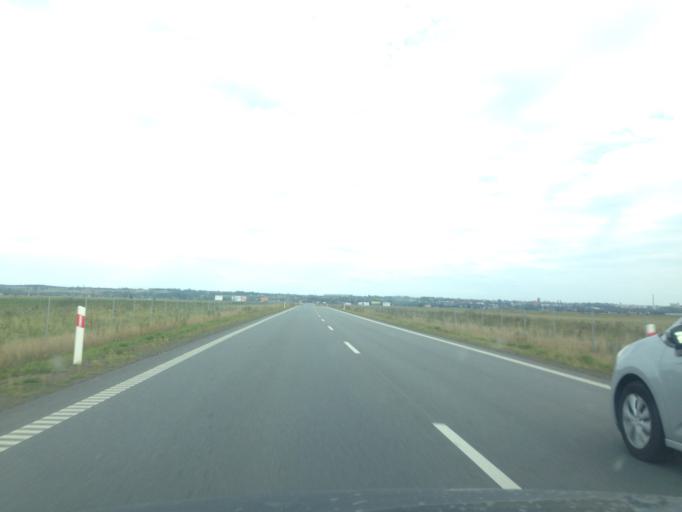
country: PL
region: Pomeranian Voivodeship
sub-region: Powiat kwidzynski
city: Kwidzyn
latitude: 53.7602
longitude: 18.8759
